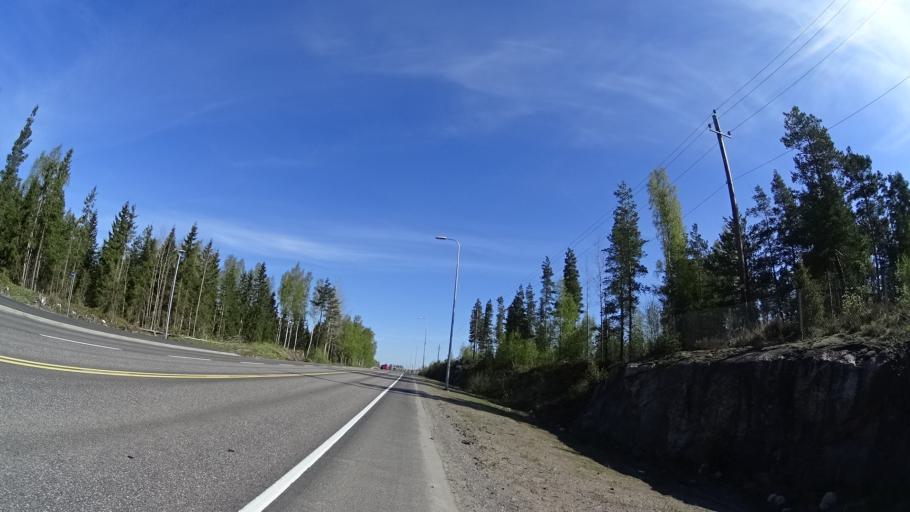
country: FI
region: Uusimaa
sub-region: Helsinki
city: Nurmijaervi
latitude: 60.4440
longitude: 24.8333
